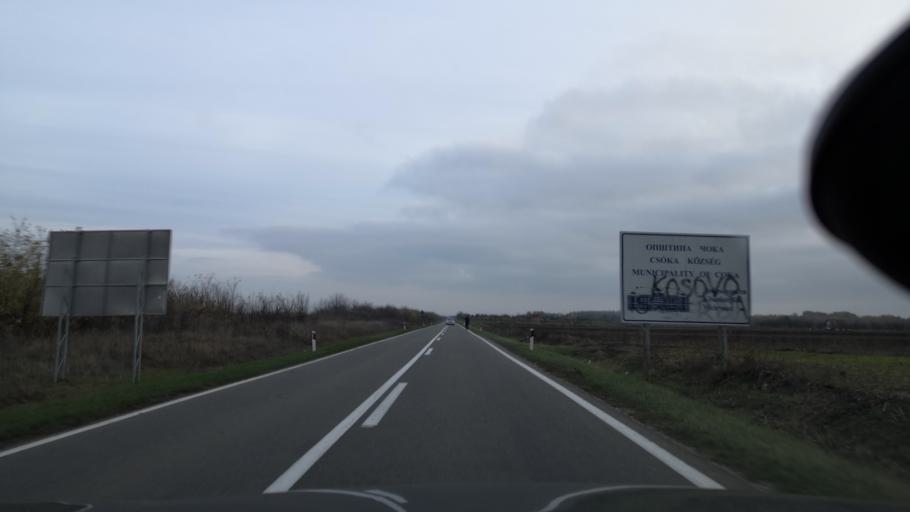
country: RS
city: Sanad
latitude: 45.9989
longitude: 20.1032
